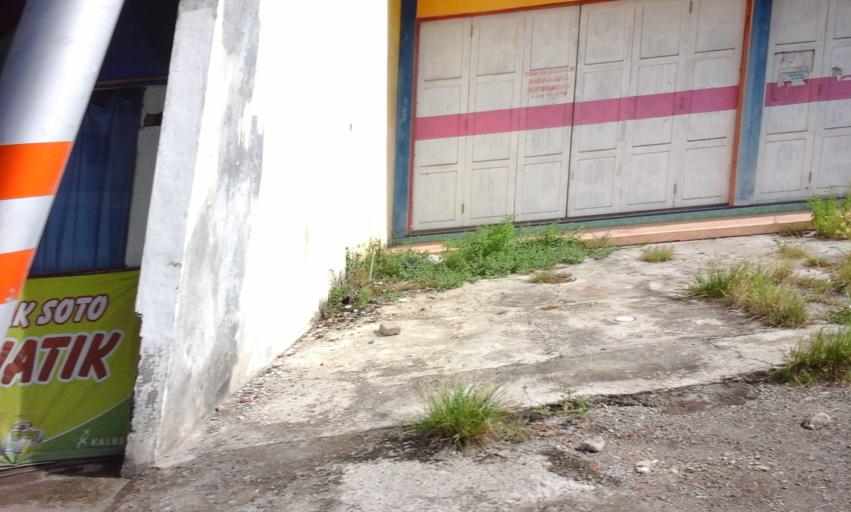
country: ID
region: East Java
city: Gaplak
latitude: -8.2143
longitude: 114.3465
